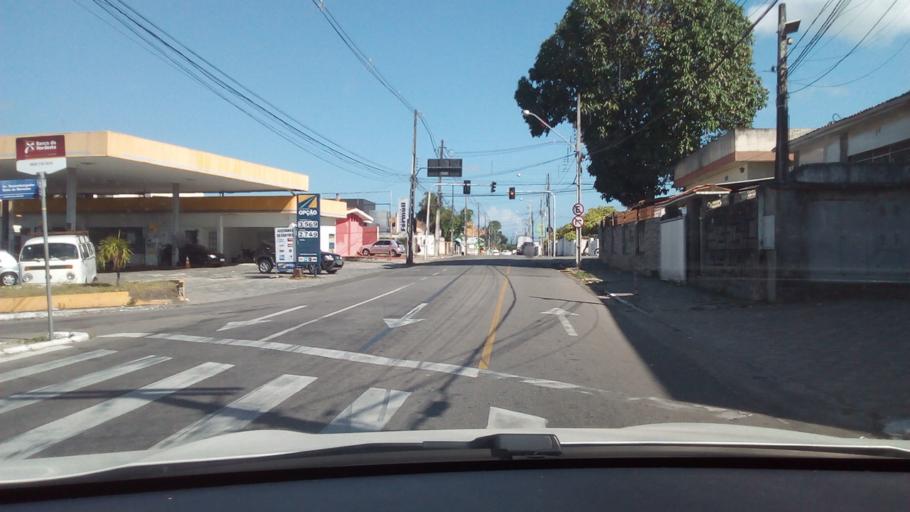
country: BR
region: Paraiba
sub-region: Joao Pessoa
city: Joao Pessoa
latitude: -7.1152
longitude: -34.8742
